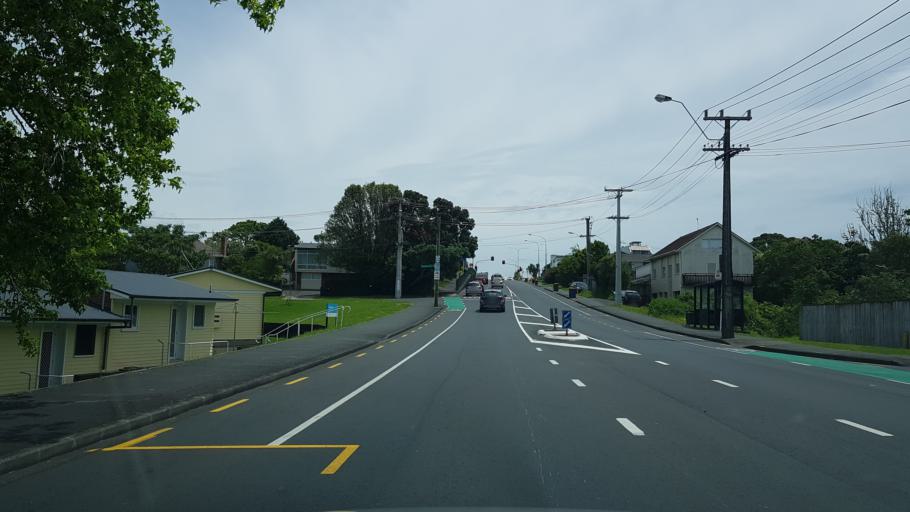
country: NZ
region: Auckland
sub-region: Auckland
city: North Shore
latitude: -36.8103
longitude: 174.7911
